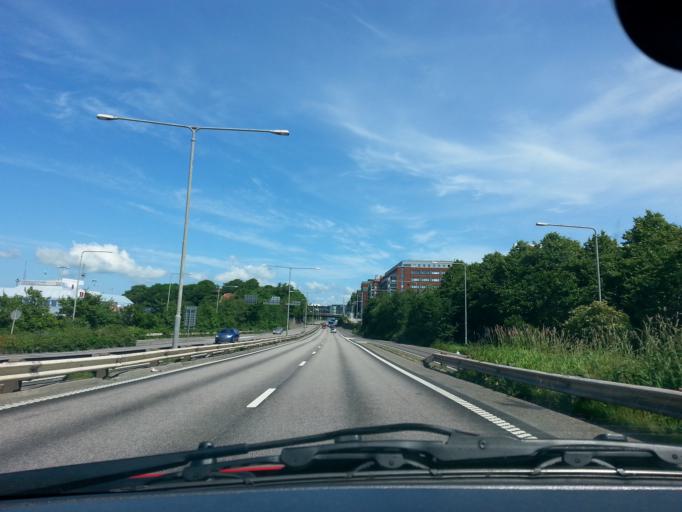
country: SE
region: Vaestra Goetaland
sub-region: Goteborg
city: Majorna
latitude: 57.6922
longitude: 11.9147
